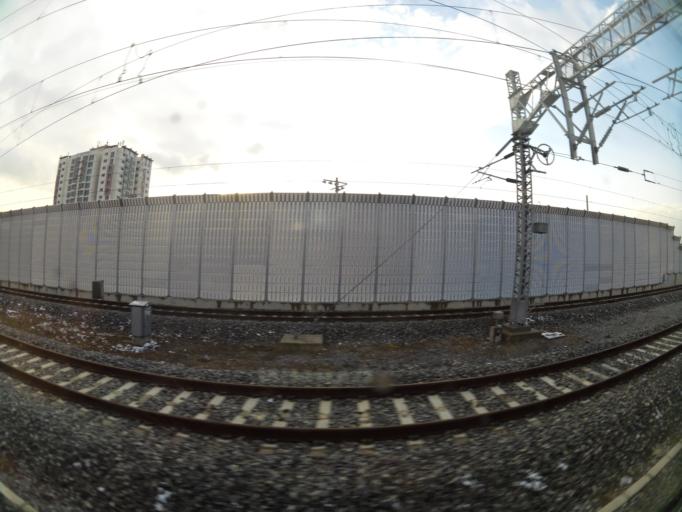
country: KR
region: Daejeon
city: Daejeon
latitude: 36.3381
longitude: 127.4312
